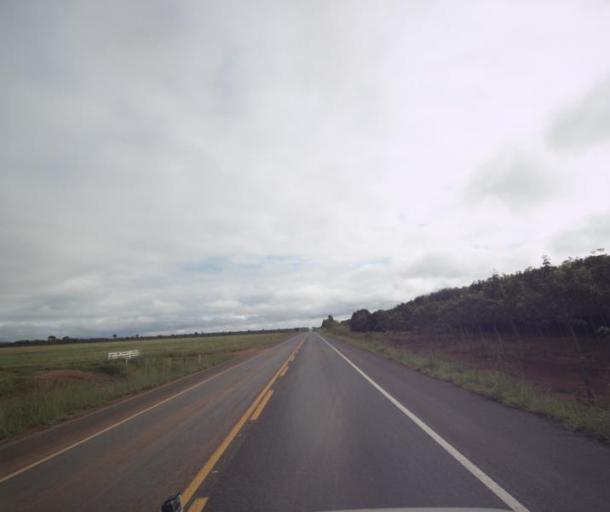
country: BR
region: Goias
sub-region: Padre Bernardo
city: Padre Bernardo
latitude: -15.3752
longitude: -48.6455
